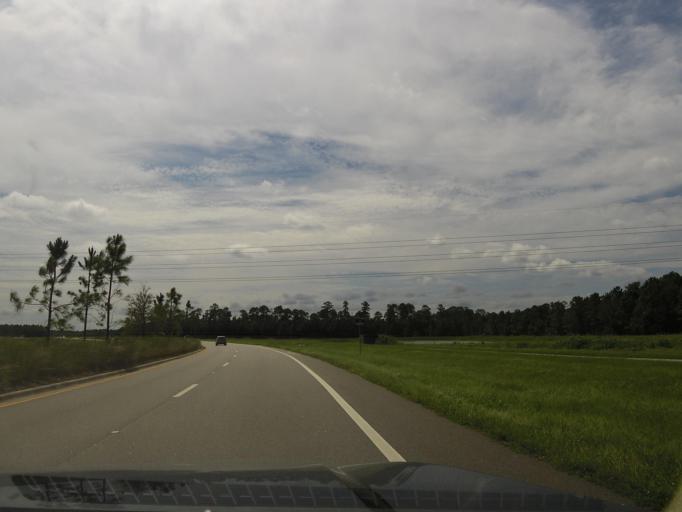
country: US
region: Florida
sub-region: Clay County
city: Green Cove Springs
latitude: 29.9865
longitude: -81.5130
